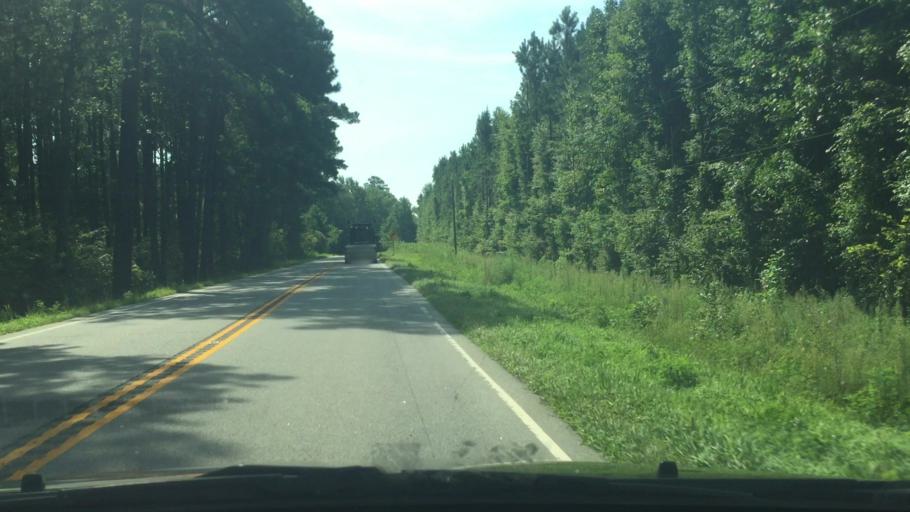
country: US
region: Virginia
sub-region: Sussex County
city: Sussex
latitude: 36.8710
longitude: -77.1444
